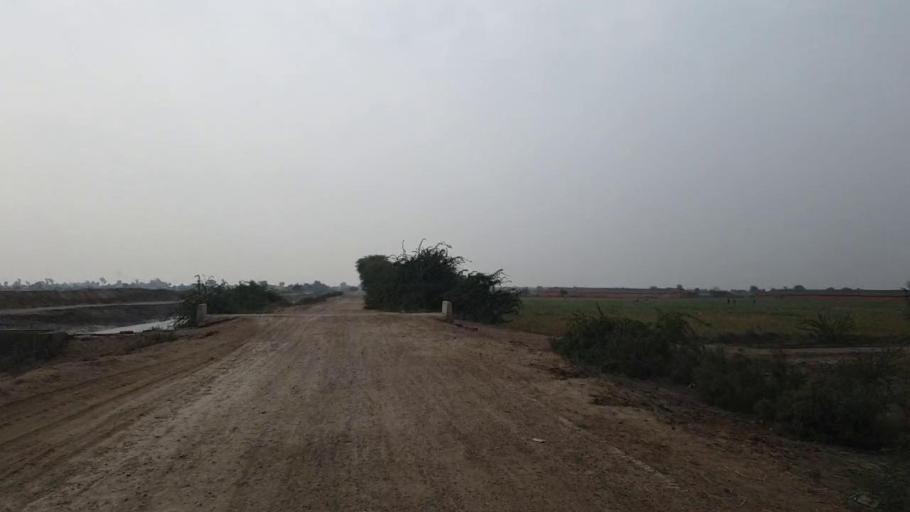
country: PK
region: Sindh
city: Kario
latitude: 24.8913
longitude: 68.5262
